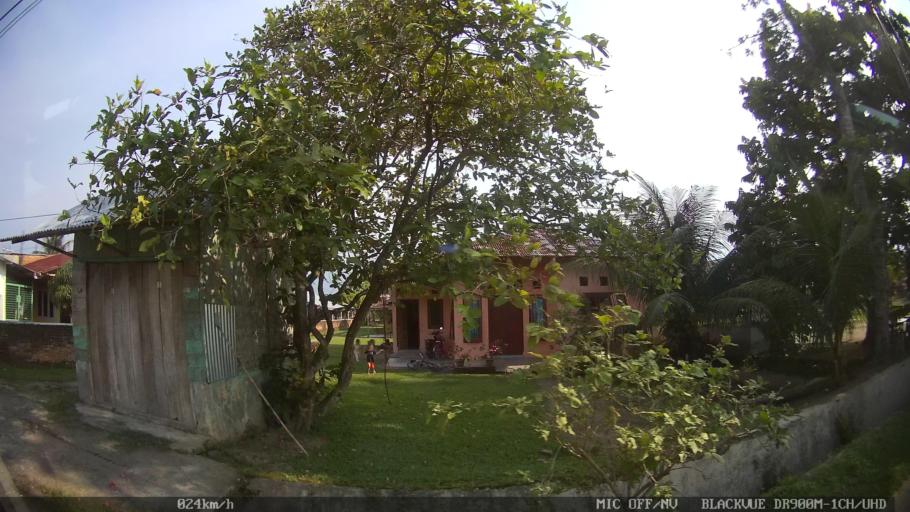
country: ID
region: North Sumatra
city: Binjai
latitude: 3.6209
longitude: 98.5253
